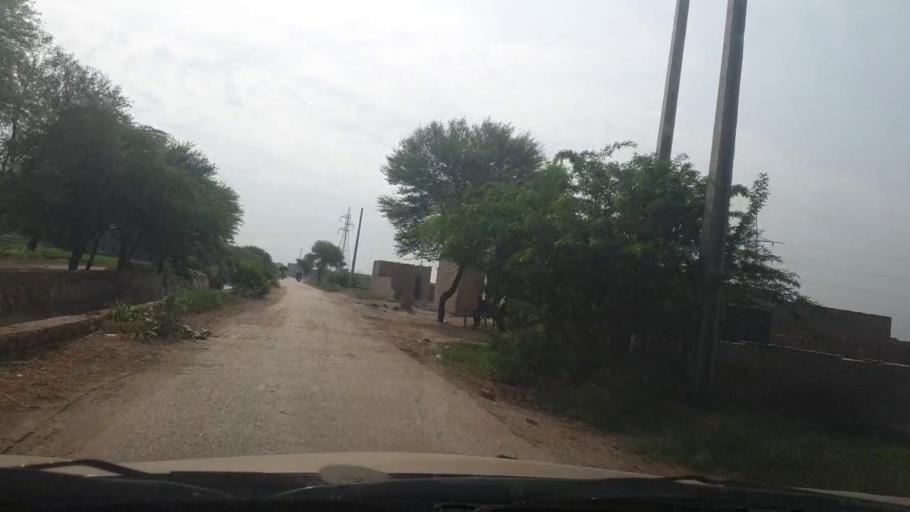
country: PK
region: Sindh
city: Larkana
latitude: 27.5823
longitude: 68.2004
